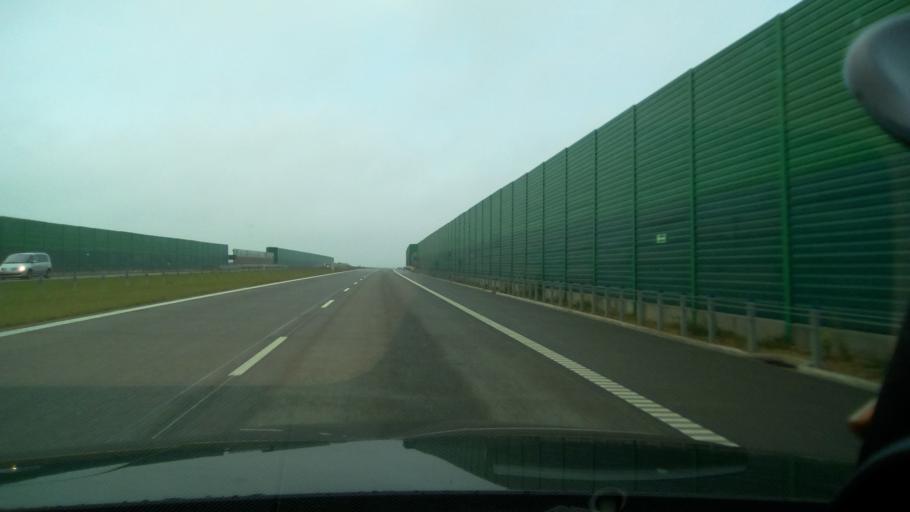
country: PL
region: Silesian Voivodeship
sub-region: Powiat klobucki
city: Kalej
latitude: 50.8253
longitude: 19.0257
